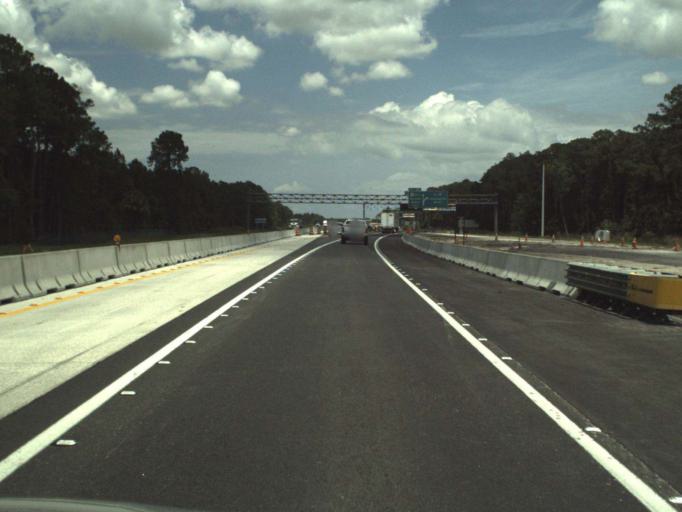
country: US
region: Florida
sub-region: Volusia County
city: Samsula-Spruce Creek
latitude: 29.1207
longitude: -81.1342
